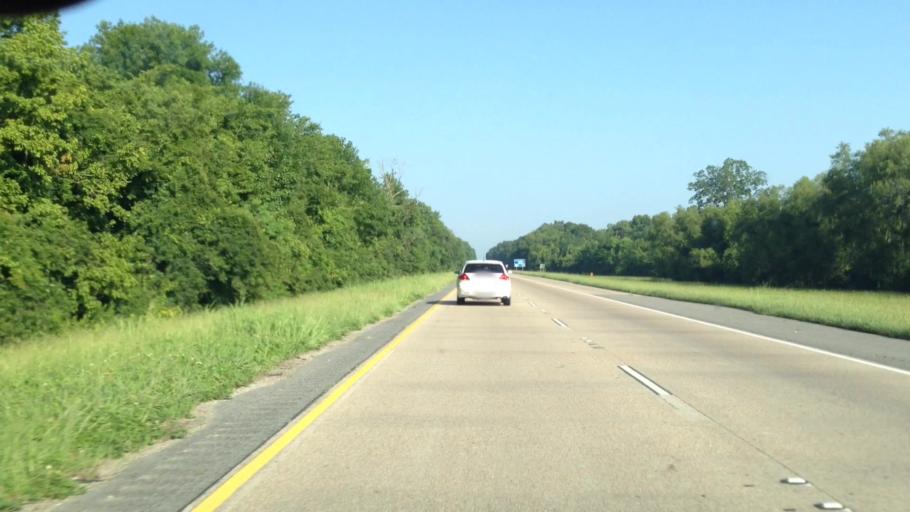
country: US
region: Louisiana
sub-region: Ascension Parish
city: Sorrento
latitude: 30.1835
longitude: -90.9013
